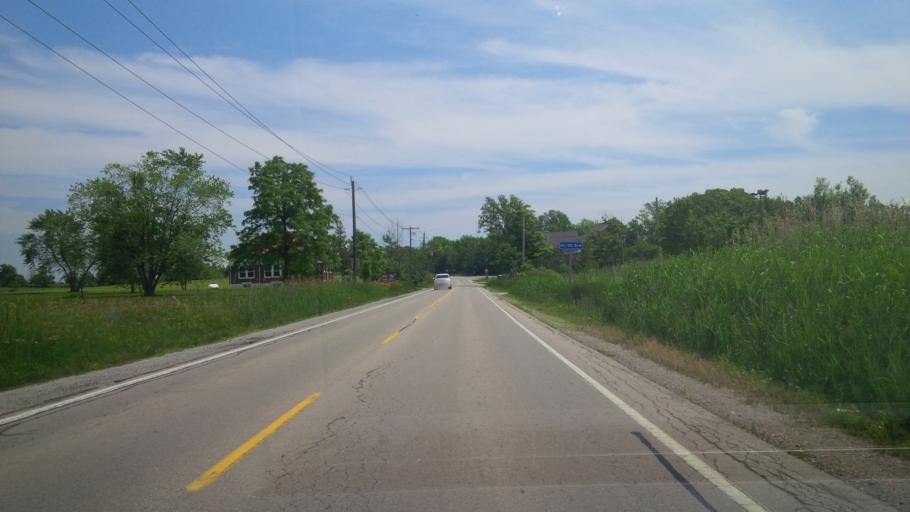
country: CA
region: Ontario
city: Burlington
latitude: 43.4305
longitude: -79.8407
